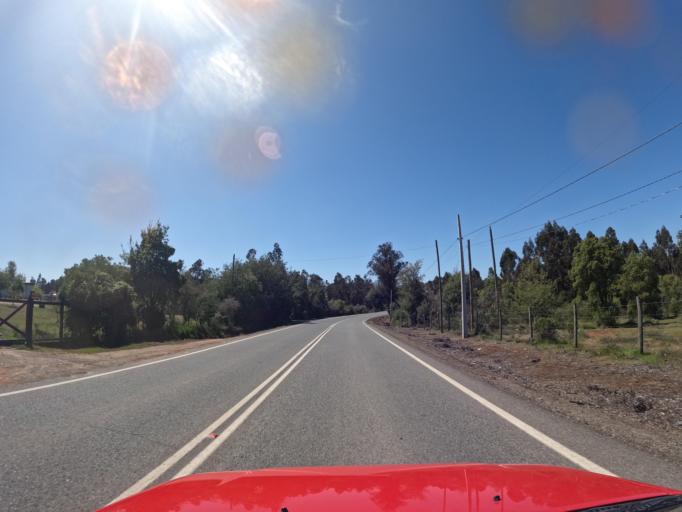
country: CL
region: Maule
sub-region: Provincia de Talca
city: San Clemente
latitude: -35.4463
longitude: -71.2686
